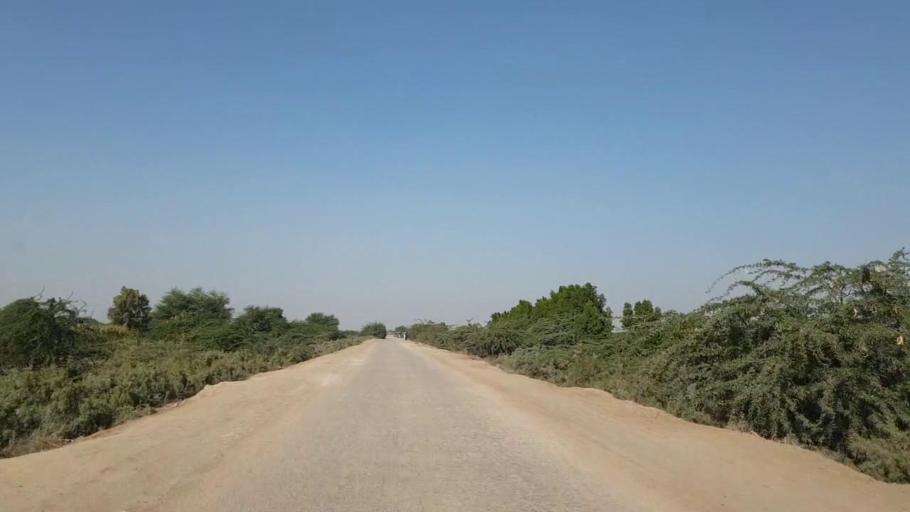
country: PK
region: Sindh
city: Digri
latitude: 25.0359
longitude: 69.1049
